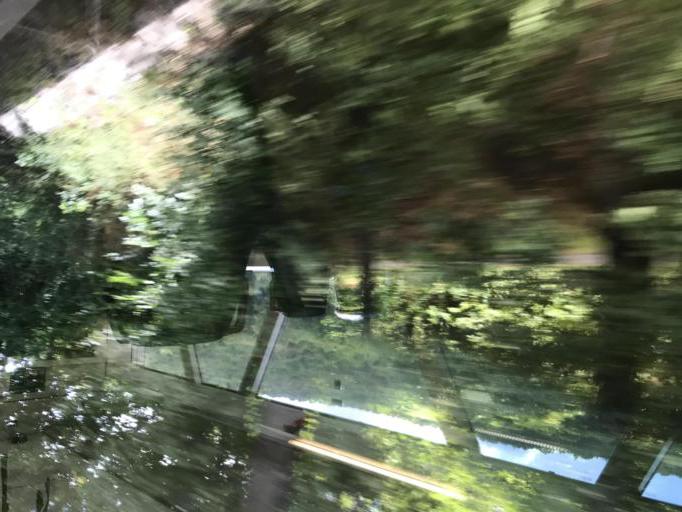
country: DE
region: Bavaria
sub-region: Regierungsbezirk Unterfranken
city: Schonau
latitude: 50.0870
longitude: 9.7214
